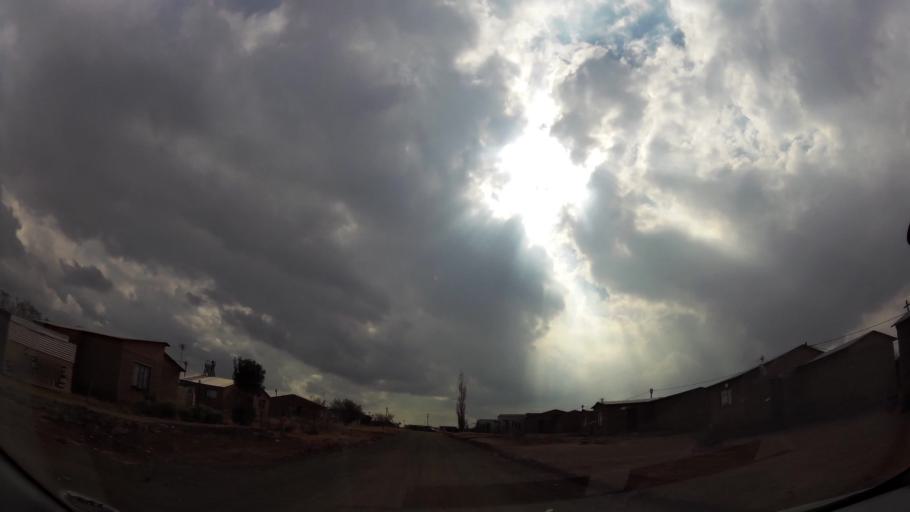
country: ZA
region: Orange Free State
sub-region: Fezile Dabi District Municipality
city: Sasolburg
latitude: -26.8572
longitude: 27.9034
